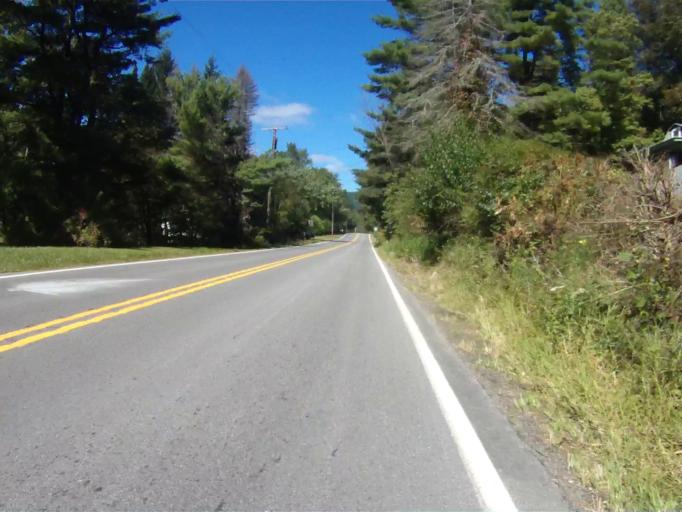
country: US
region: Pennsylvania
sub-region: Centre County
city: Milesburg
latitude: 40.9180
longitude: -77.8921
